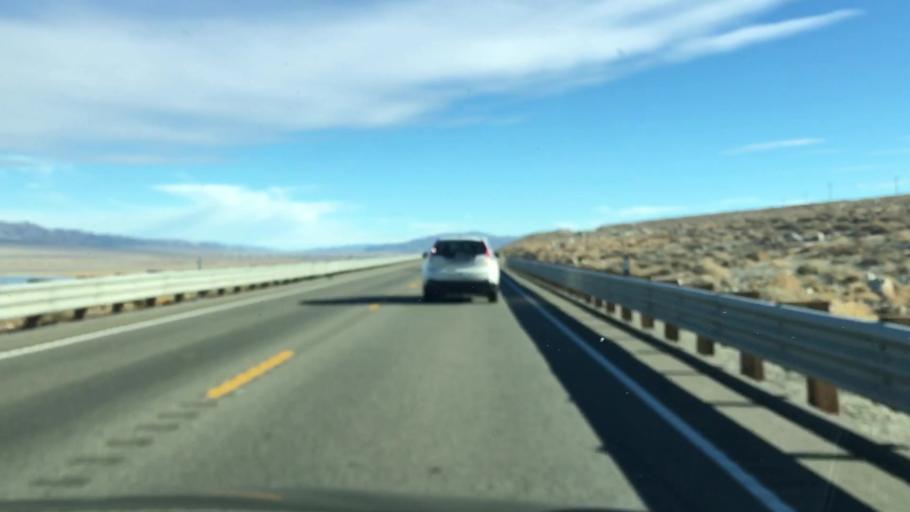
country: US
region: Nevada
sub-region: Mineral County
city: Hawthorne
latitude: 38.6157
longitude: -118.7284
